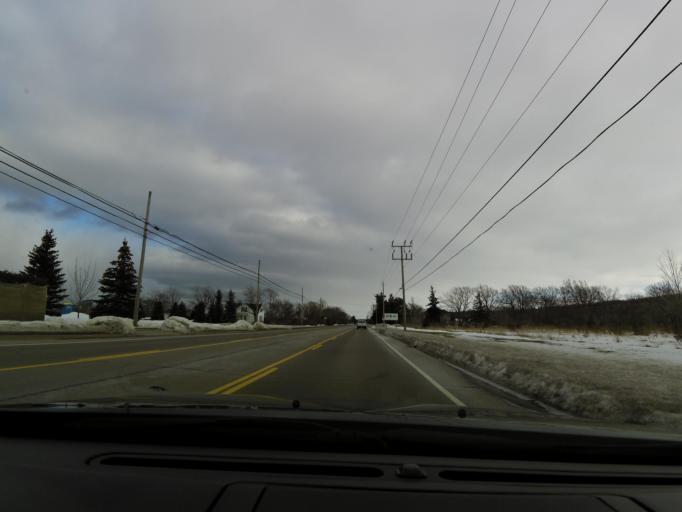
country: CA
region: Ontario
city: Hamilton
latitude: 43.2059
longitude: -79.6237
